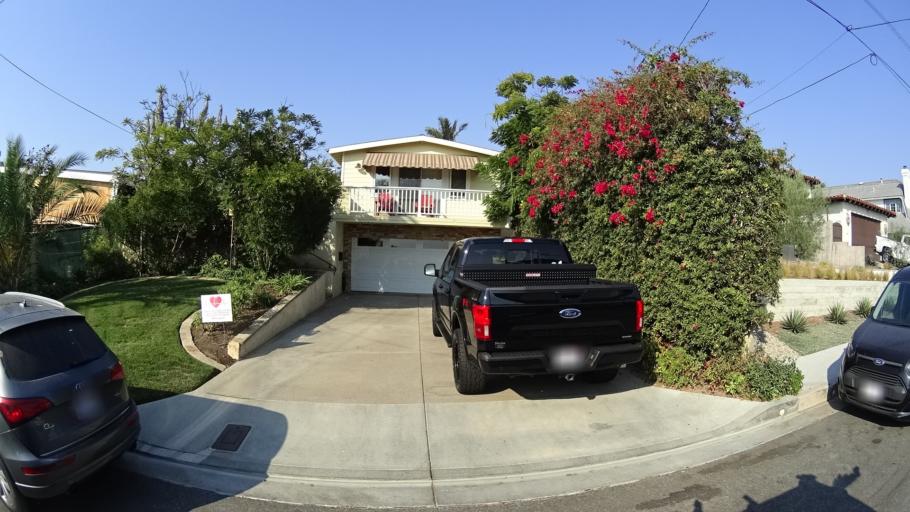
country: US
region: California
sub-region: Orange County
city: San Clemente
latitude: 33.4115
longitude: -117.6093
